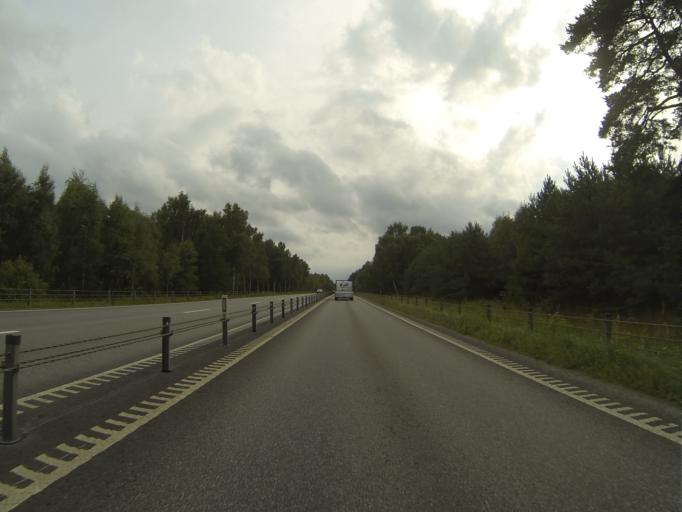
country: SE
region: Skane
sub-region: Kristianstads Kommun
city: Norra Asum
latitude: 55.9753
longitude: 14.0816
